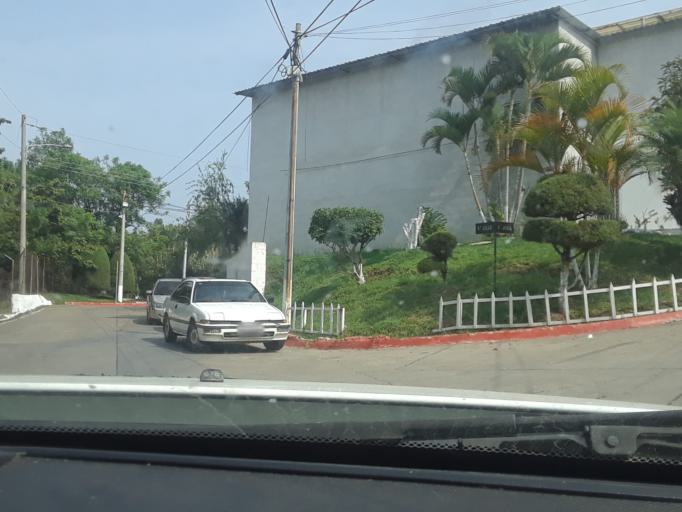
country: GT
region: Guatemala
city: Petapa
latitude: 14.5346
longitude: -90.5540
